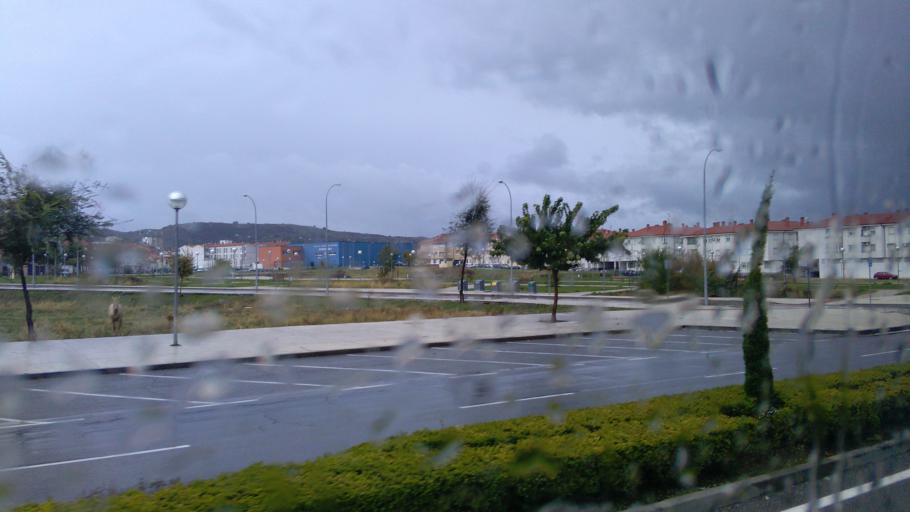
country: ES
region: Extremadura
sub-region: Provincia de Caceres
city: Navalmoral de la Mata
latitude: 39.8933
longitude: -5.5315
